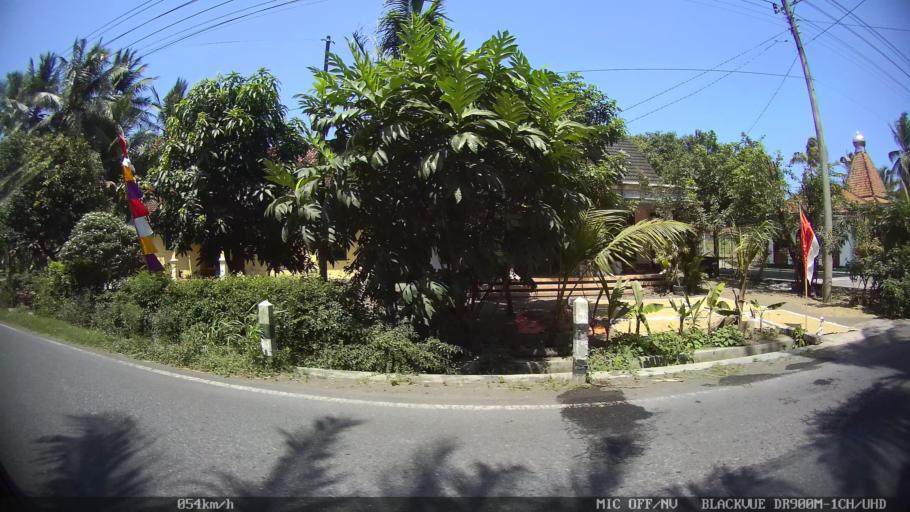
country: ID
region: Daerah Istimewa Yogyakarta
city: Srandakan
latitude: -7.9272
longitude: 110.1280
